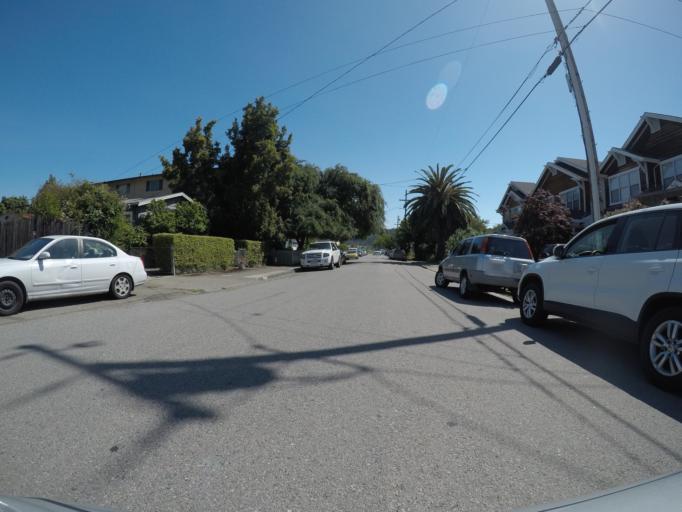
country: US
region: California
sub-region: Marin County
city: San Rafael
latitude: 37.9728
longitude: -122.5143
